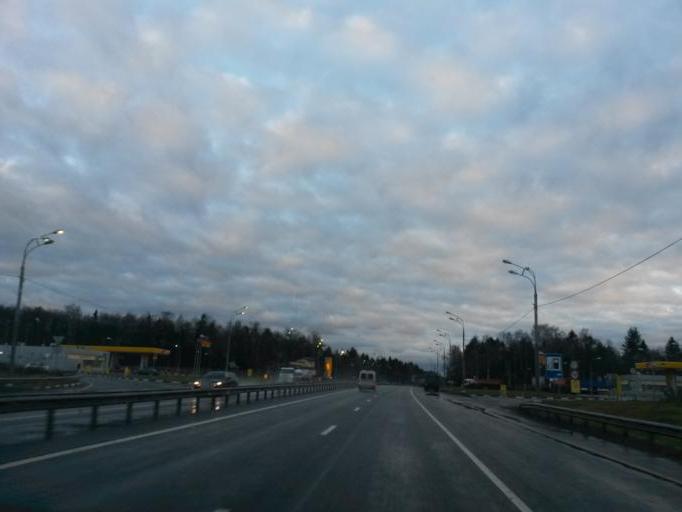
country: RU
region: Moskovskaya
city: Svatkovo
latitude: 56.3422
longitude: 38.2647
